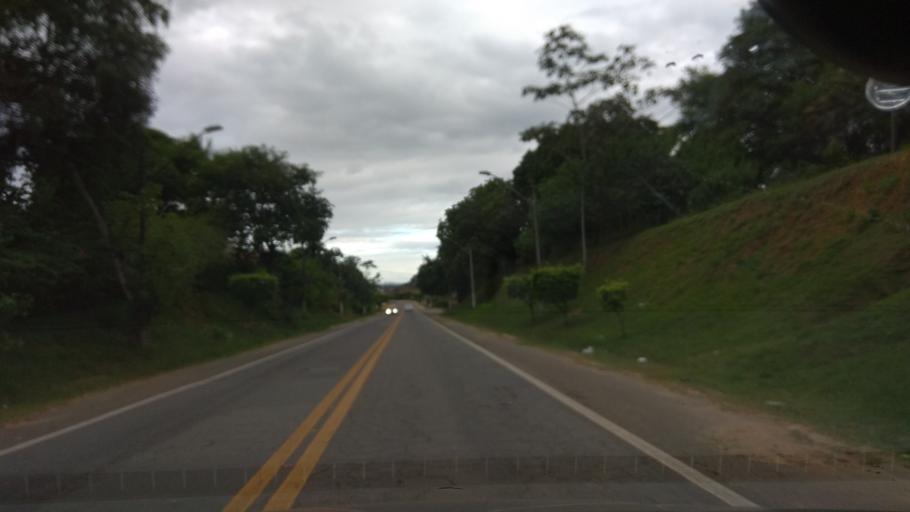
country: BR
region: Bahia
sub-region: Ubata
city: Ubata
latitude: -14.2053
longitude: -39.5301
